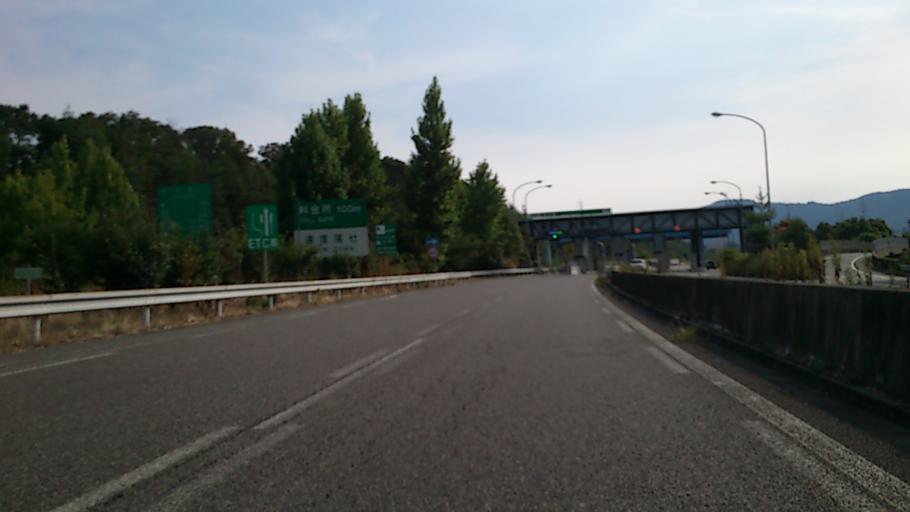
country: JP
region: Shiga Prefecture
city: Kusatsu
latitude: 34.9681
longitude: 135.9269
